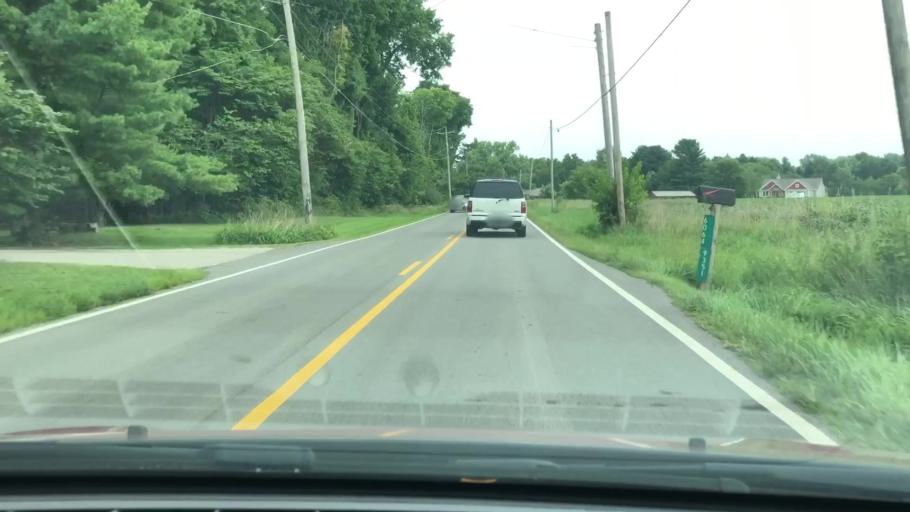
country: US
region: Ohio
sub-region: Franklin County
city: New Albany
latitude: 40.1481
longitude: -82.8403
